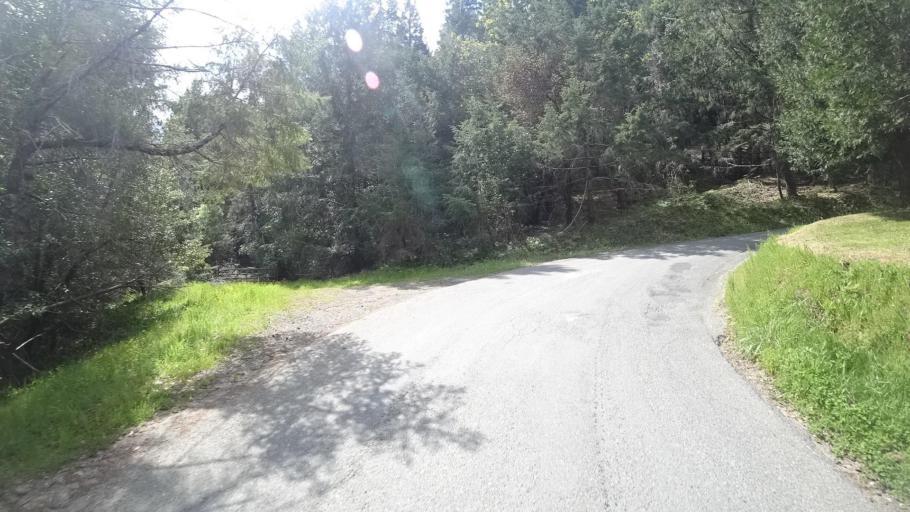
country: US
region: California
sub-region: Humboldt County
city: Redway
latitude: 40.0667
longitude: -123.8296
